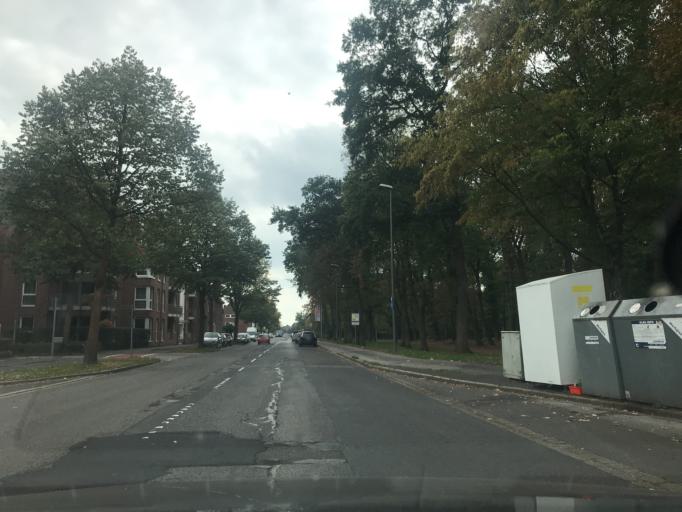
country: DE
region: North Rhine-Westphalia
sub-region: Regierungsbezirk Dusseldorf
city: Krefeld
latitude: 51.3631
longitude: 6.6392
